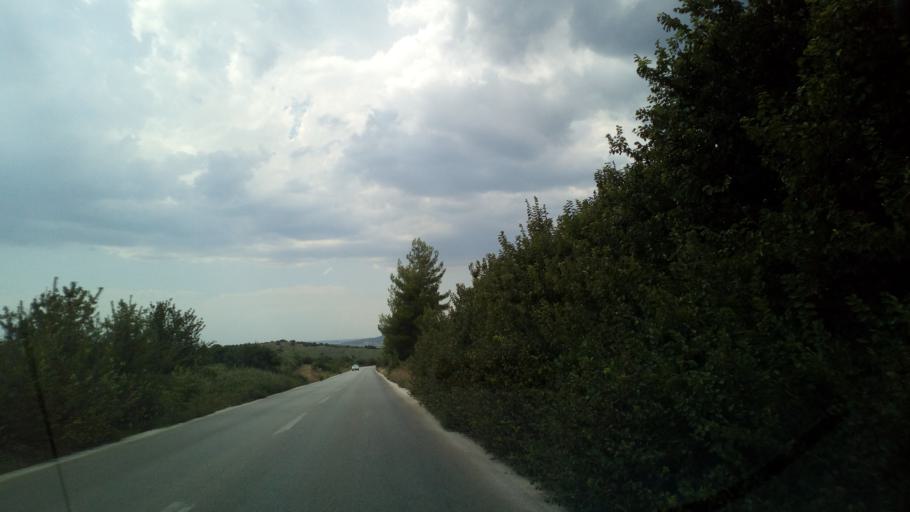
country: GR
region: Central Macedonia
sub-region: Nomos Chalkidikis
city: Ormylia
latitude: 40.2510
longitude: 23.5710
